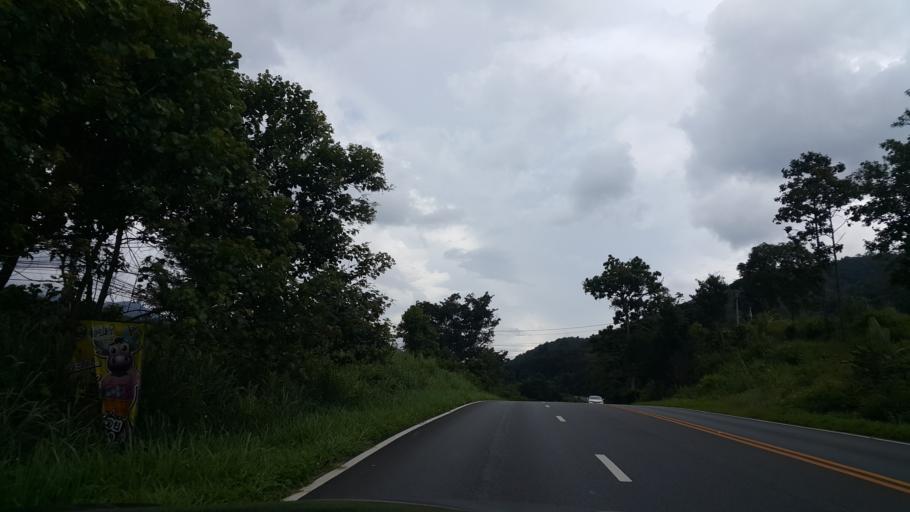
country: TH
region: Chiang Mai
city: Mae On
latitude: 19.0242
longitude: 99.3141
